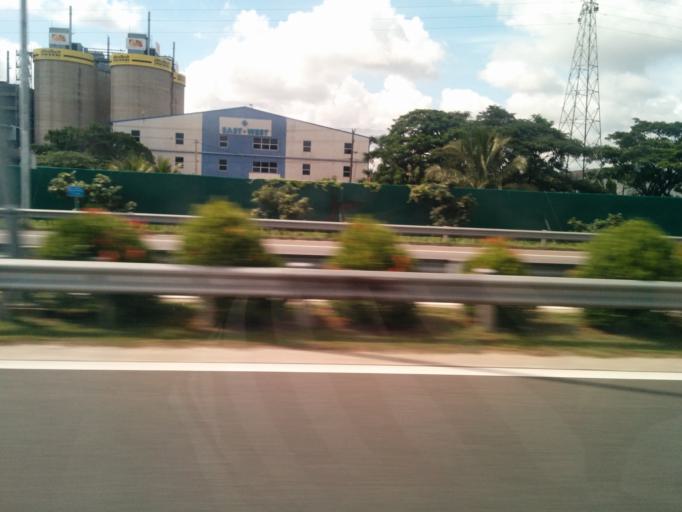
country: LK
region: Western
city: Peliyagoda
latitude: 6.9629
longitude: 79.8892
